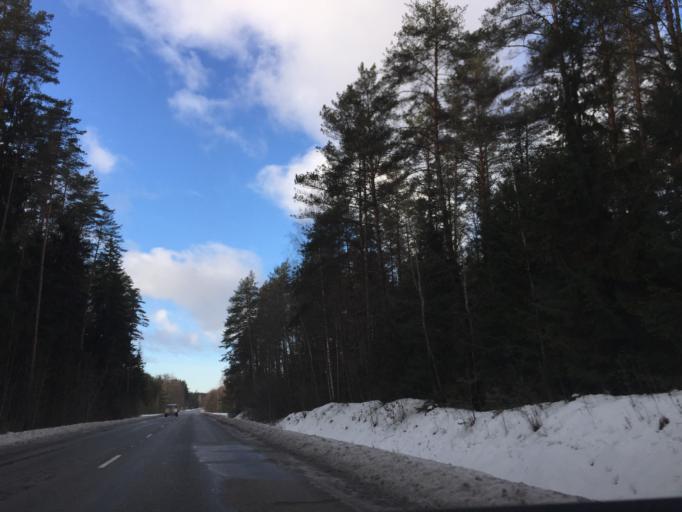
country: LV
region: Ogre
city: Jumprava
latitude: 56.6300
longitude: 24.9162
